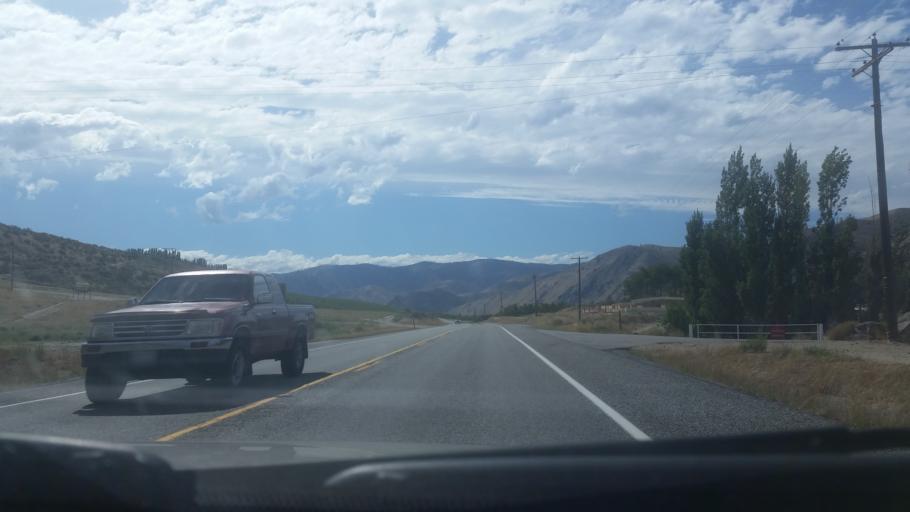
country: US
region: Washington
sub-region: Chelan County
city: Manson
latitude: 47.7683
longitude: -120.1192
